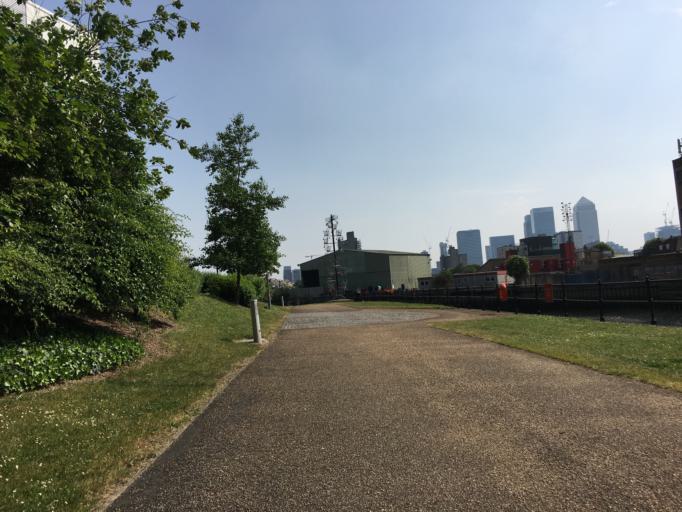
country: GB
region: England
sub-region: Greater London
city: Poplar
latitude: 51.5207
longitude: -0.0086
